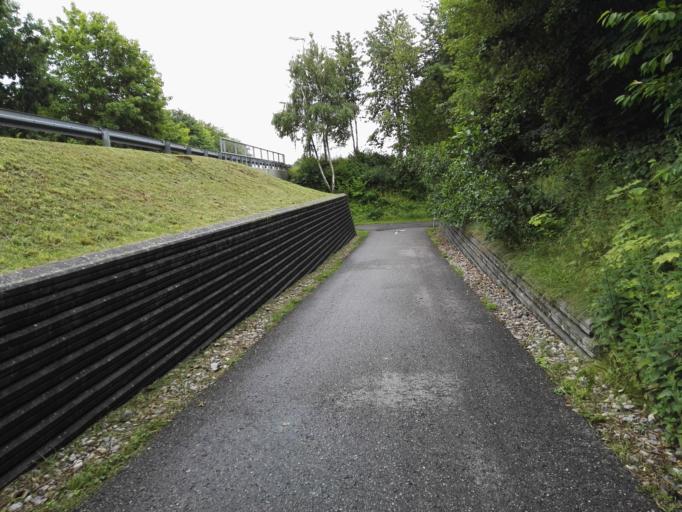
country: DK
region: Capital Region
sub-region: Egedal Kommune
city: Olstykke
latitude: 55.7727
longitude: 12.1650
